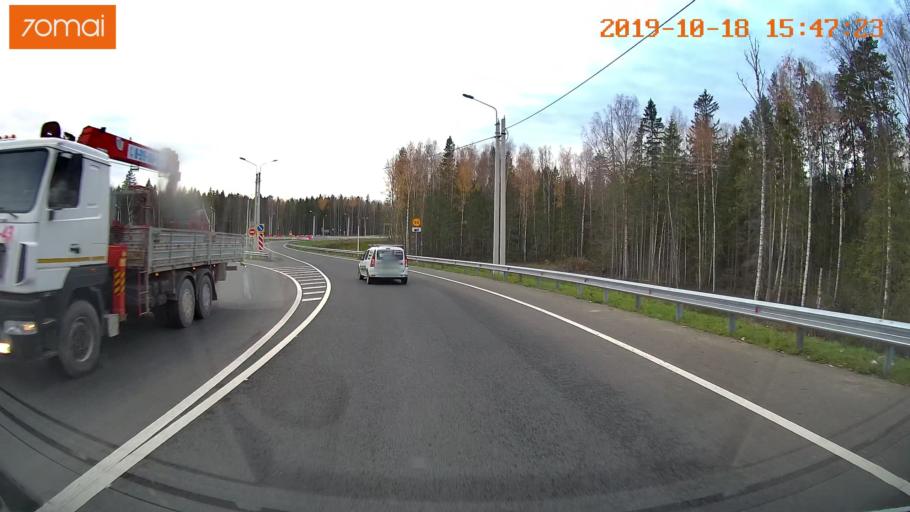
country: RU
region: Vladimir
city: Kommunar
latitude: 56.0171
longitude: 40.5745
